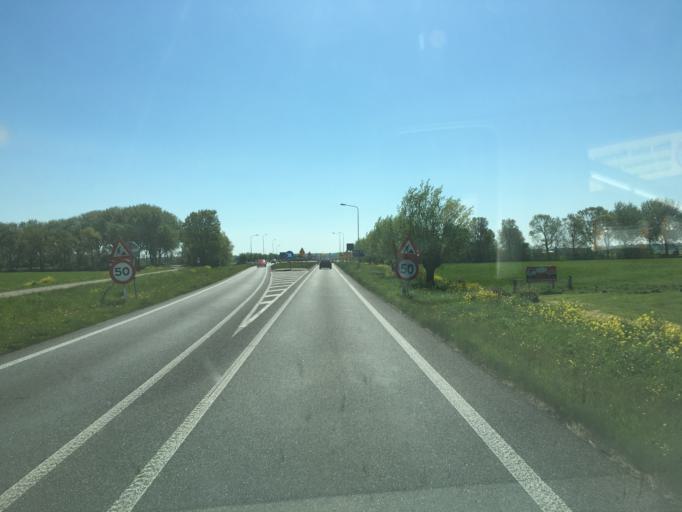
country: NL
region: Friesland
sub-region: Sudwest Fryslan
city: Koudum
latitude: 52.8897
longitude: 5.4808
